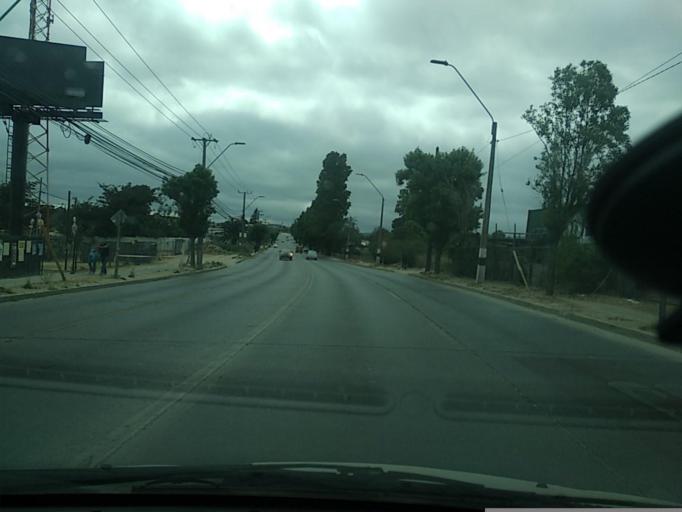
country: CL
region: Valparaiso
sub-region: Provincia de Marga Marga
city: Villa Alemana
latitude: -33.0462
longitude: -71.3982
